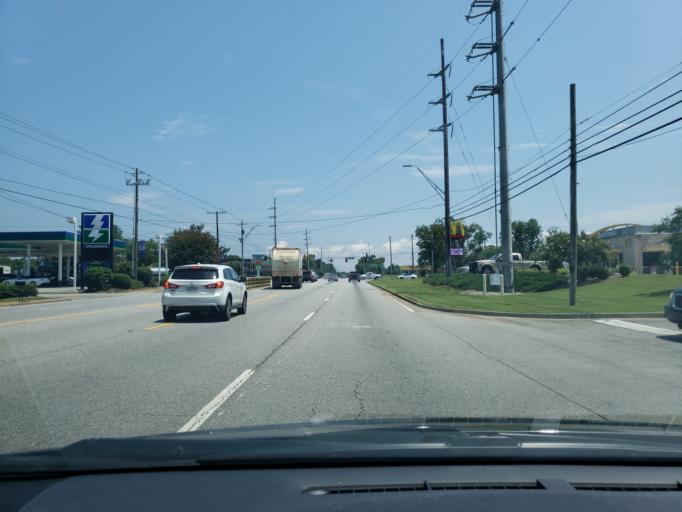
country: US
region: Georgia
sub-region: Dougherty County
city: Albany
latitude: 31.5856
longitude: -84.2208
